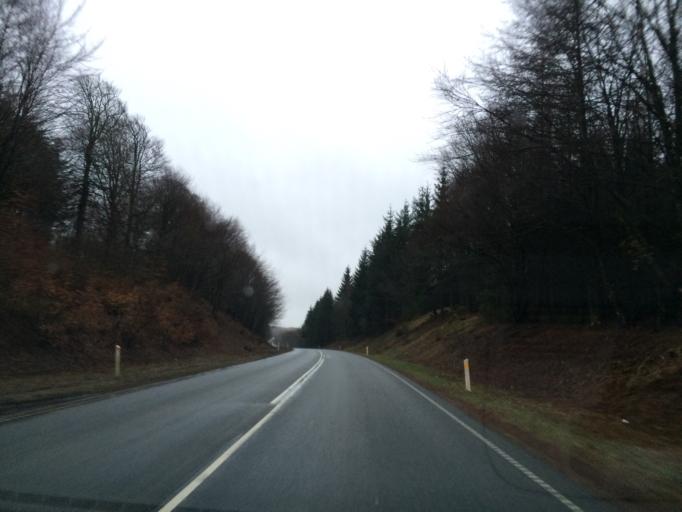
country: DK
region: North Denmark
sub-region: Mariagerfjord Kommune
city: Arden
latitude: 56.8025
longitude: 9.8172
